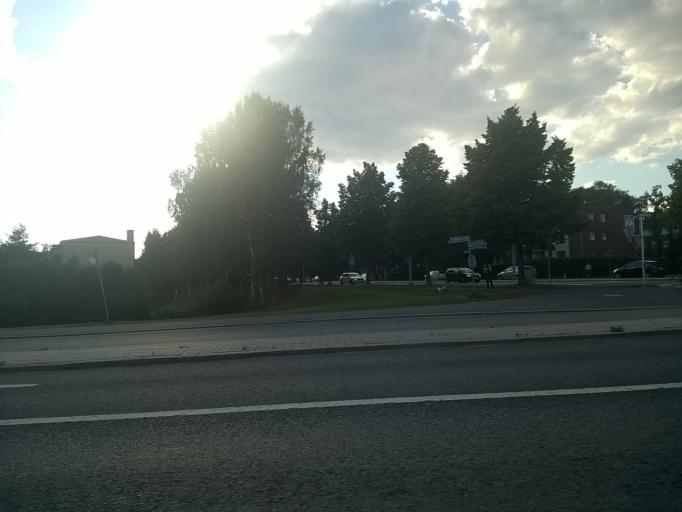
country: FI
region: Pirkanmaa
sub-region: Tampere
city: Tampere
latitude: 61.4740
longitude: 23.7647
